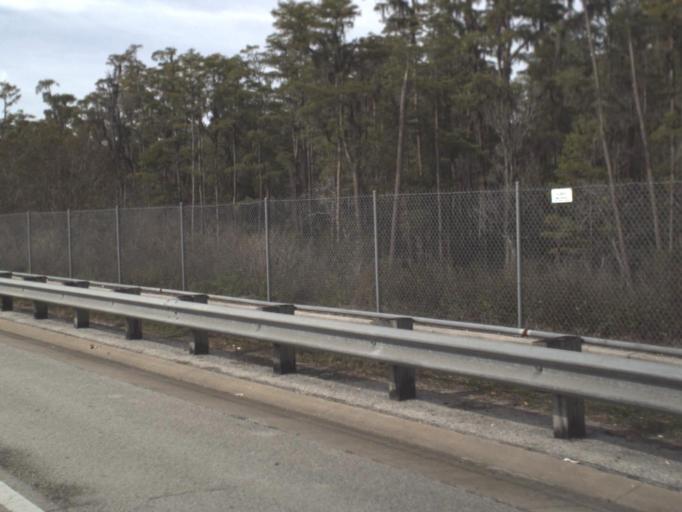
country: US
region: Florida
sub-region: Orange County
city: Oak Ridge
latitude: 28.4592
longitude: -81.4243
